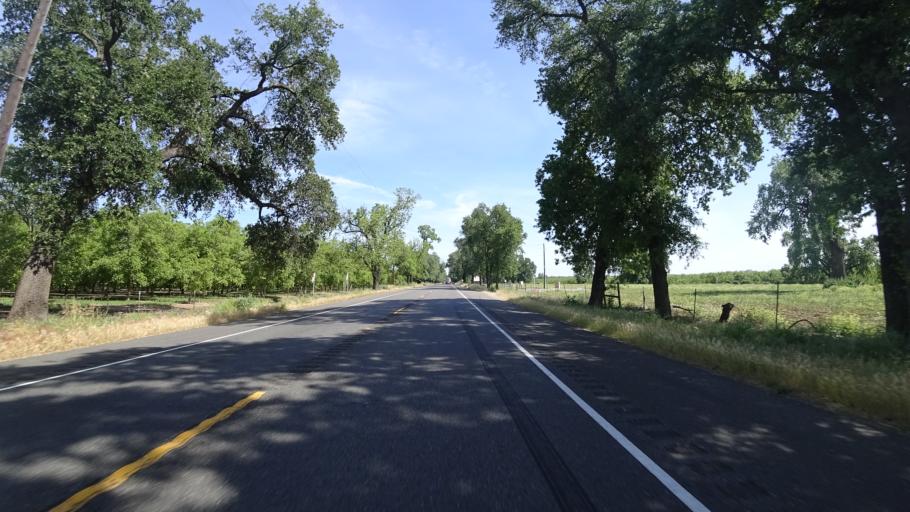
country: US
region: California
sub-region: Tehama County
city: Red Bluff
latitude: 40.1763
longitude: -122.1686
